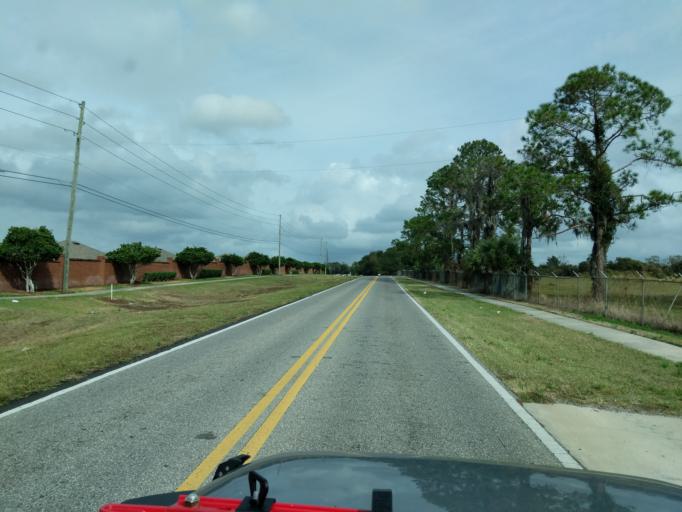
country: US
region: Florida
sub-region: Orange County
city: Paradise Heights
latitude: 28.6084
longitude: -81.5489
